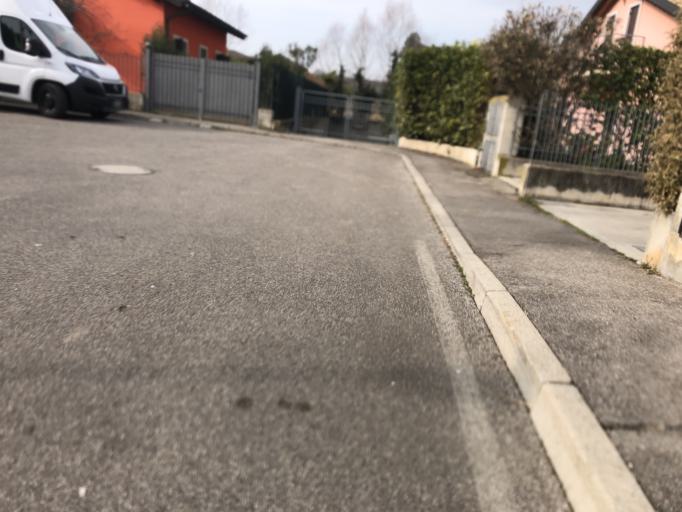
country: IT
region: Veneto
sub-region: Provincia di Verona
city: Sona
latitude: 45.4242
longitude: 10.8246
